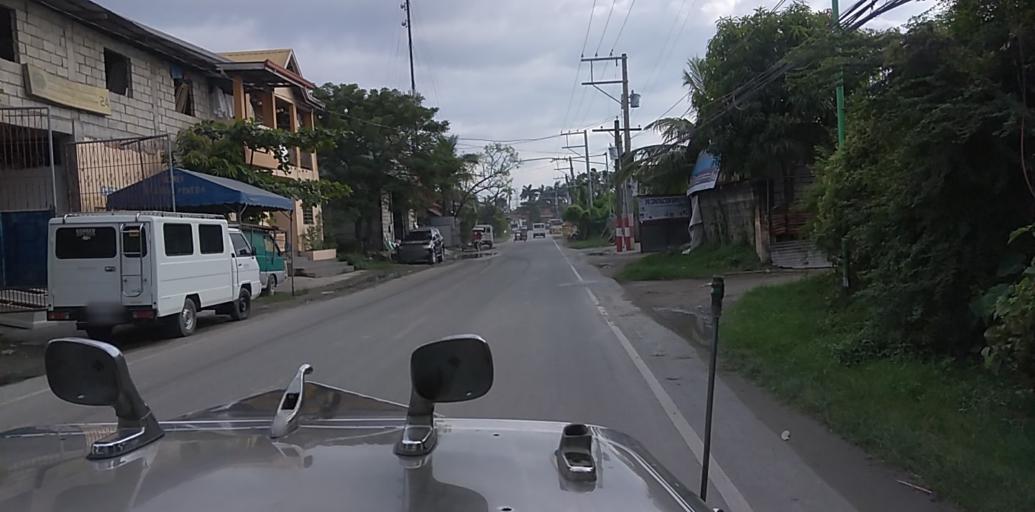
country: PH
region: Central Luzon
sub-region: Province of Pampanga
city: Minalin
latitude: 14.9901
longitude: 120.7044
